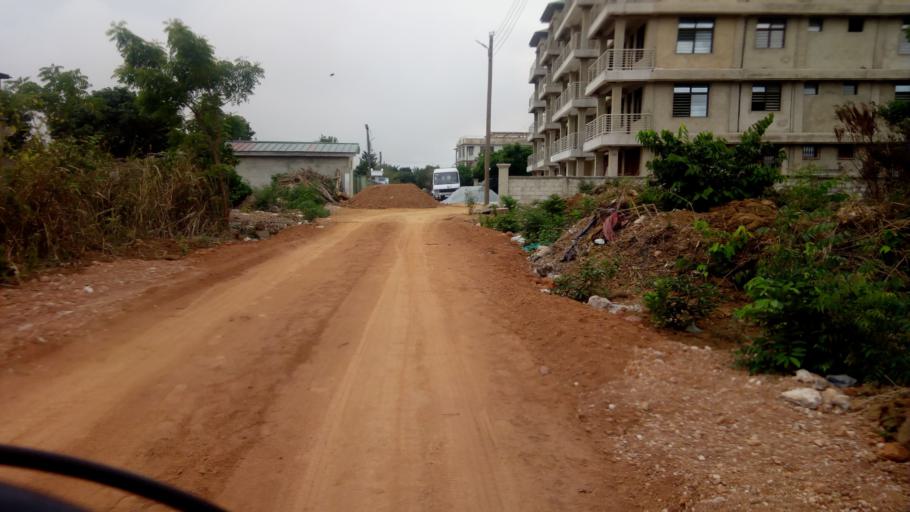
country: GH
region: Central
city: Cape Coast
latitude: 5.1095
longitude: -1.2754
